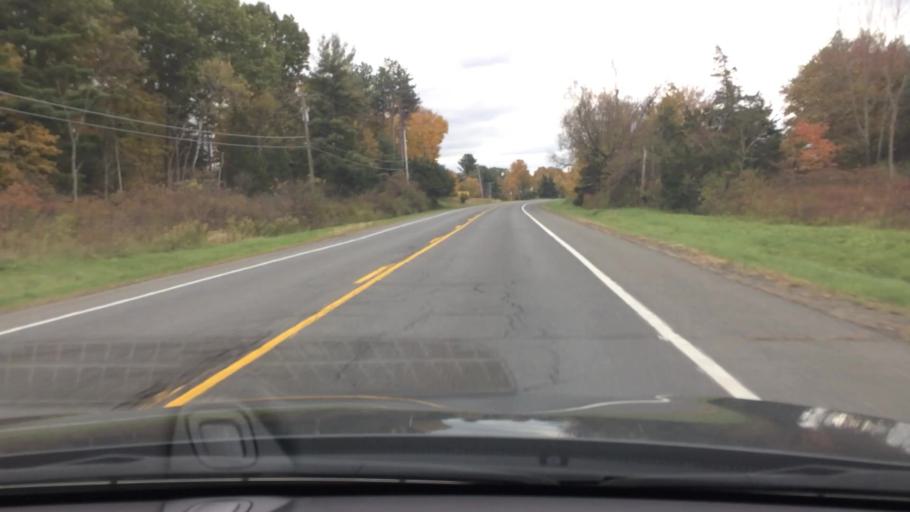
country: US
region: New York
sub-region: Columbia County
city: Oakdale
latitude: 42.1614
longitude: -73.7479
